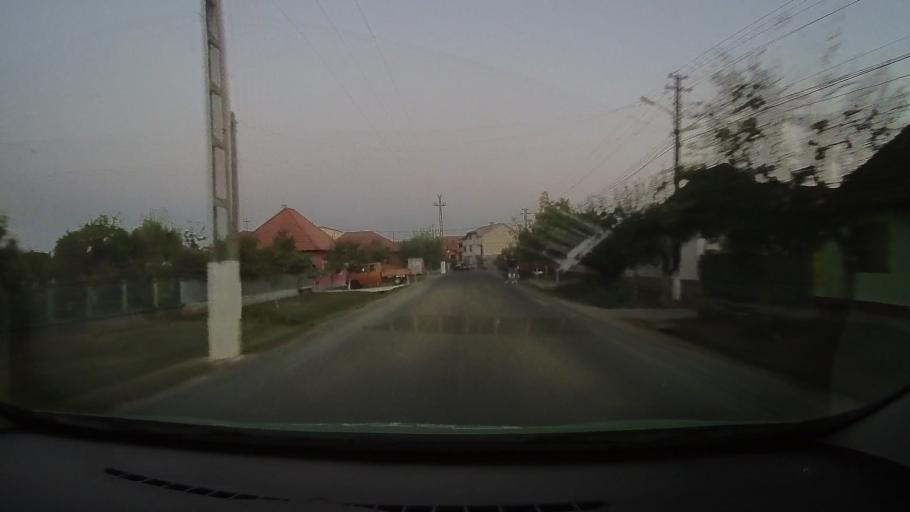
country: RO
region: Arad
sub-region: Comuna Livada
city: Livada
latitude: 46.2262
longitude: 21.3816
